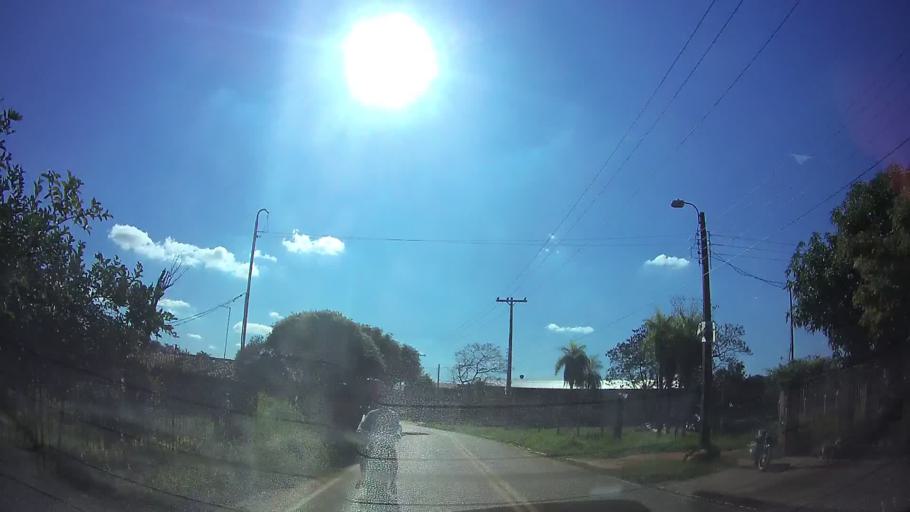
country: PY
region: Central
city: Limpio
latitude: -25.2150
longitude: -57.4762
